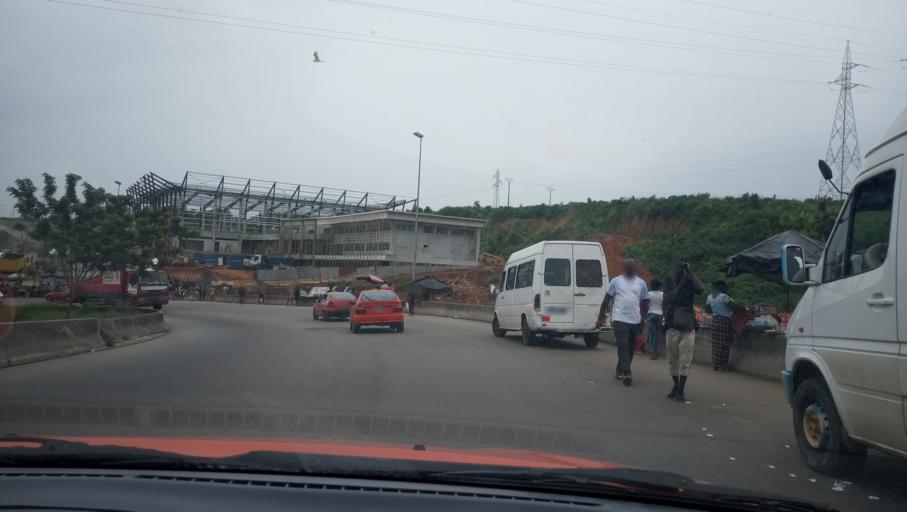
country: CI
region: Lagunes
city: Abidjan
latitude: 5.3528
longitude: -4.0128
